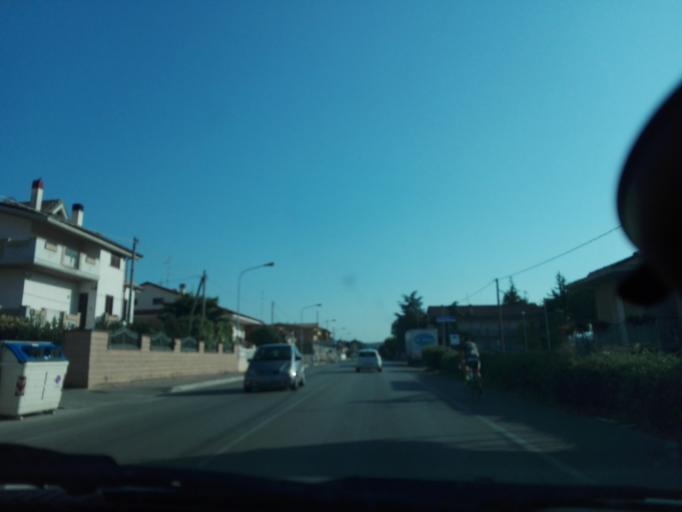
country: IT
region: Abruzzo
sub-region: Provincia di Pescara
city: Cappelle sul Tavo
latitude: 42.4925
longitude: 14.1241
